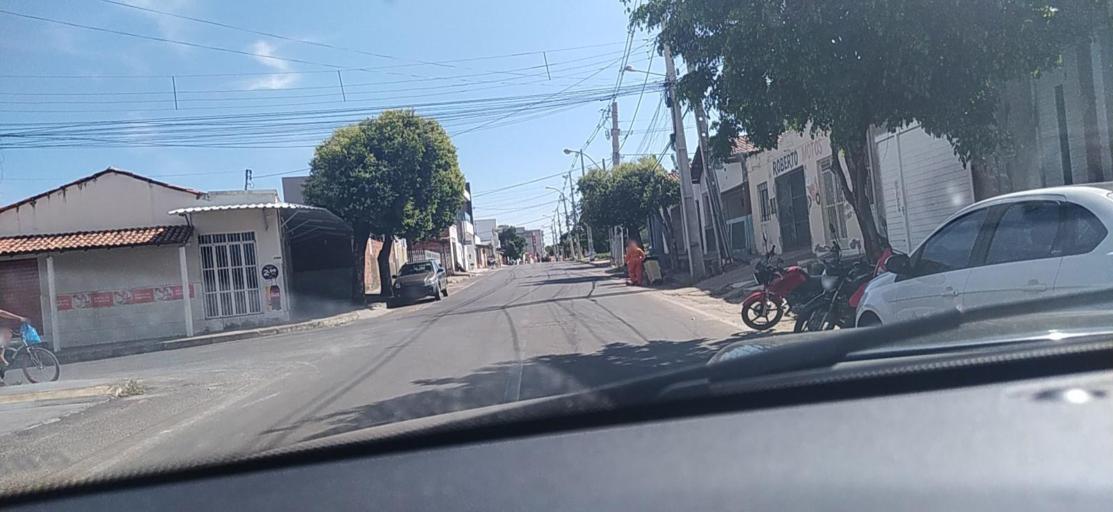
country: BR
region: Bahia
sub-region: Guanambi
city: Guanambi
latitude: -14.2185
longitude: -42.7725
